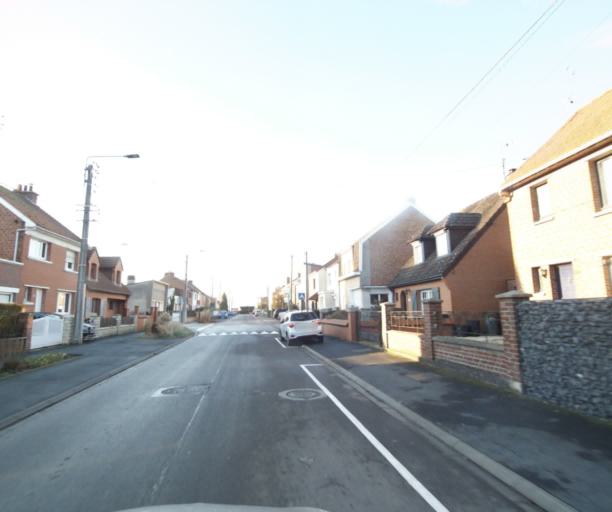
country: FR
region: Nord-Pas-de-Calais
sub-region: Departement du Nord
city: Famars
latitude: 50.3316
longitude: 3.5120
